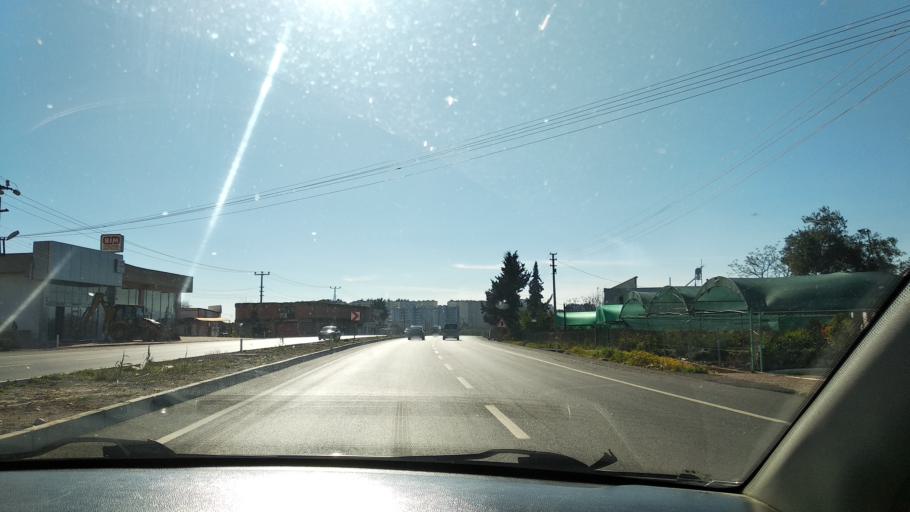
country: TR
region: Mersin
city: Tomuk
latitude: 36.6574
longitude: 34.3925
